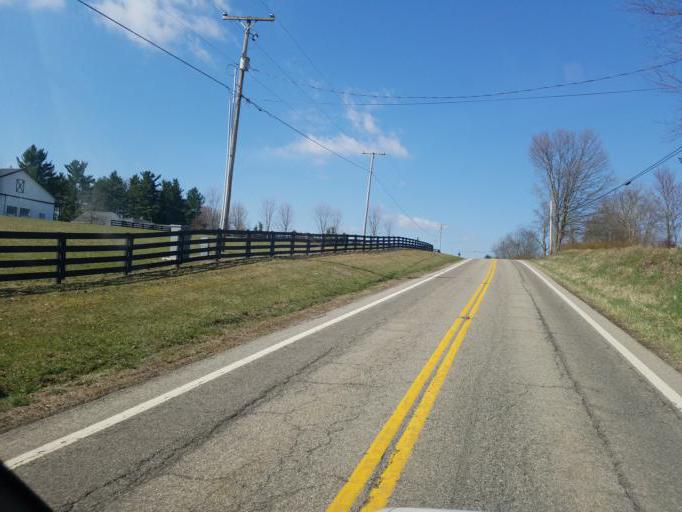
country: US
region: Ohio
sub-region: Knox County
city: Gambier
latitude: 40.2804
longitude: -82.3129
